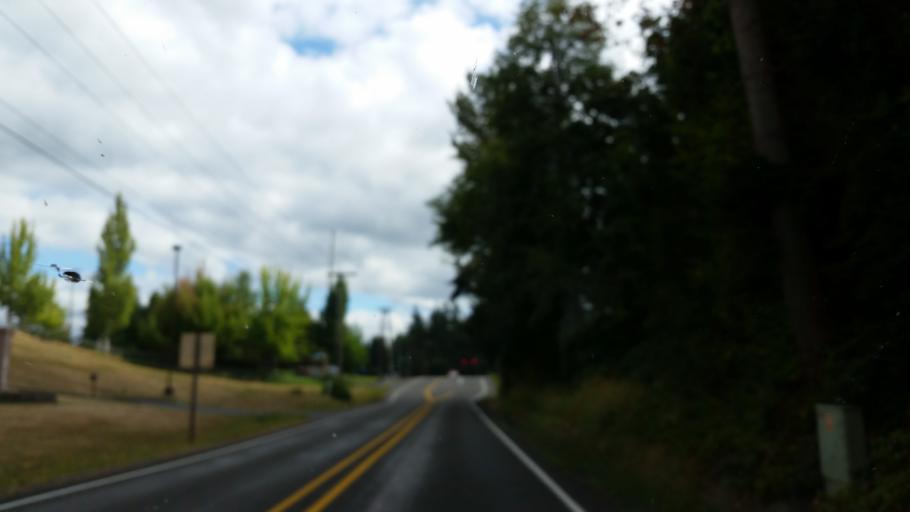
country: US
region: Washington
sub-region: Pierce County
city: Sumner
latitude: 47.2299
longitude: -122.2028
